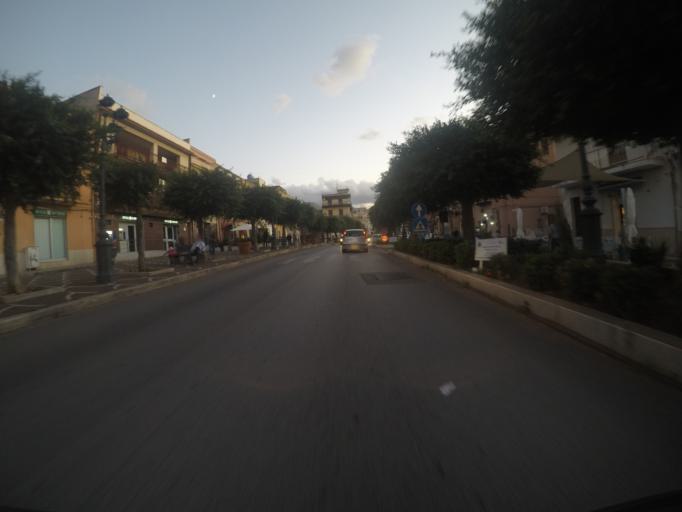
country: IT
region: Sicily
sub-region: Palermo
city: Capaci
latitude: 38.1718
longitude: 13.2398
